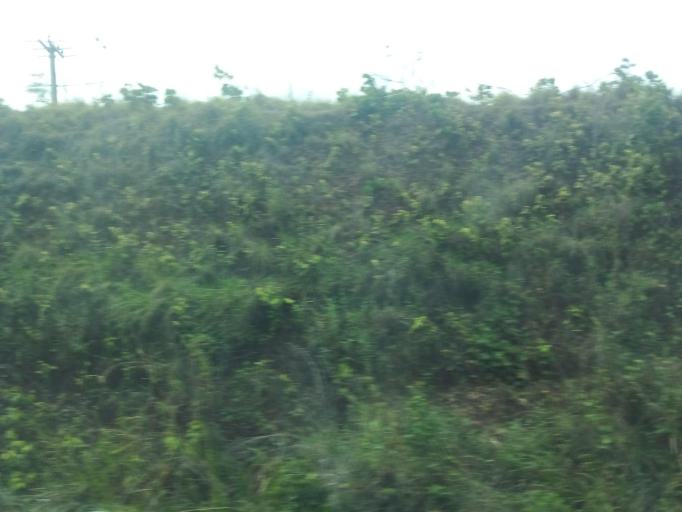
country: BR
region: Maranhao
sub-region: Santa Ines
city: Santa Ines
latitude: -3.6905
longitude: -45.9112
